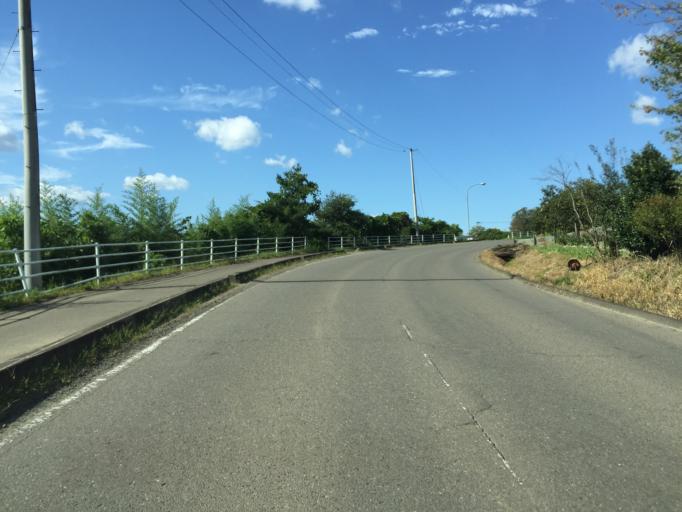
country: JP
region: Fukushima
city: Yanagawamachi-saiwaicho
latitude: 37.8503
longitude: 140.6137
